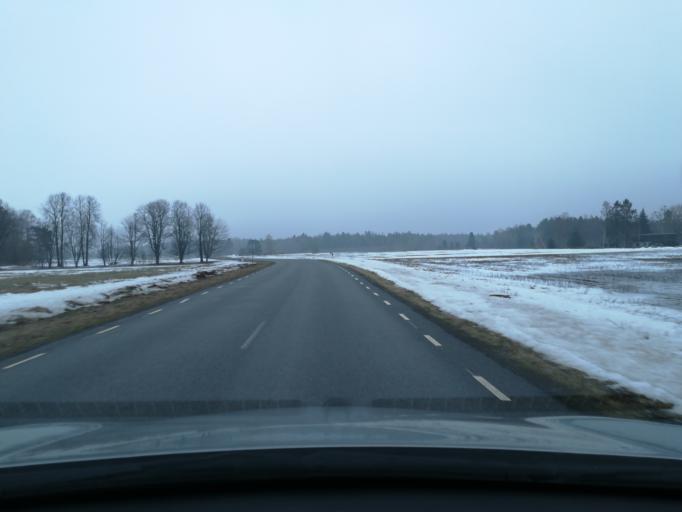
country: EE
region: Harju
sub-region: Kuusalu vald
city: Kuusalu
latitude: 59.4708
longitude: 25.5675
